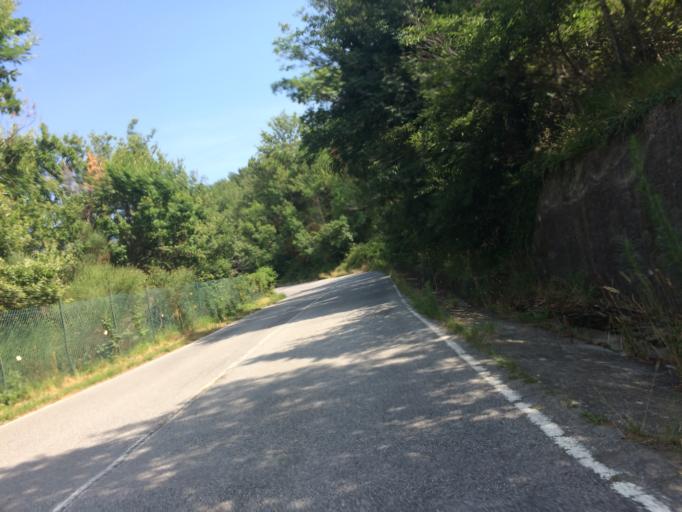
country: IT
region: Liguria
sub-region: Provincia di Savona
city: Varazze
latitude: 44.3859
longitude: 8.5679
